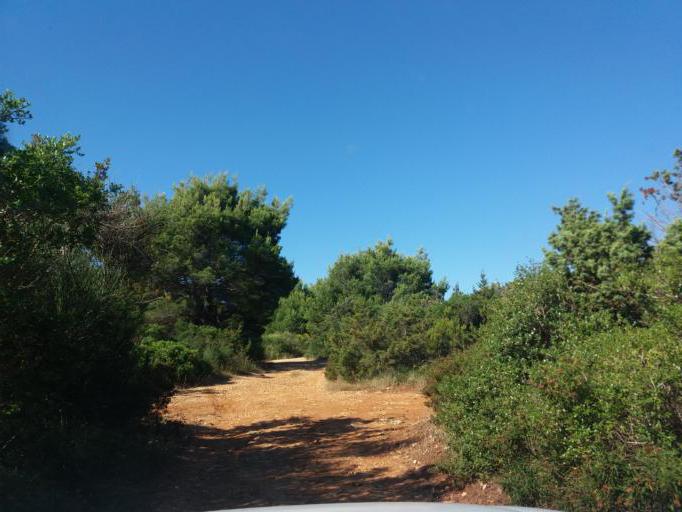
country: HR
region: Zadarska
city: Ugljan
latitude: 44.1550
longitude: 14.8235
